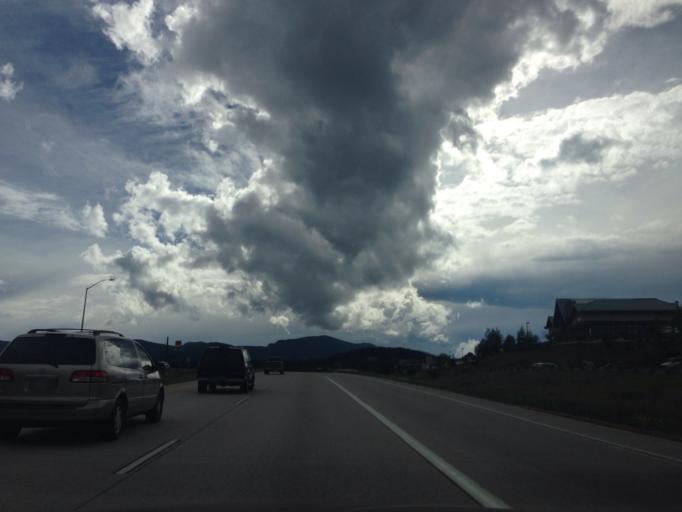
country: US
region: Colorado
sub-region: Jefferson County
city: Indian Hills
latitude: 39.5430
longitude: -105.2895
